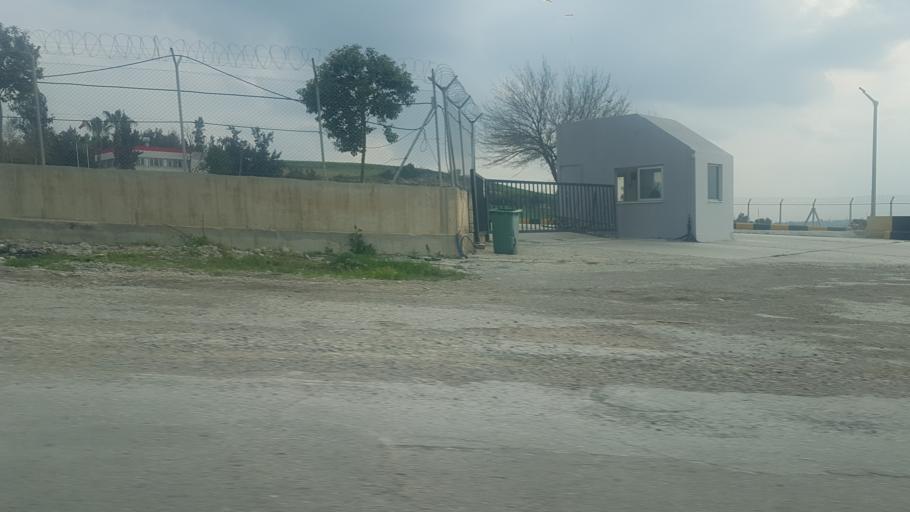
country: TR
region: Adana
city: Seyhan
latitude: 37.0442
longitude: 35.1825
